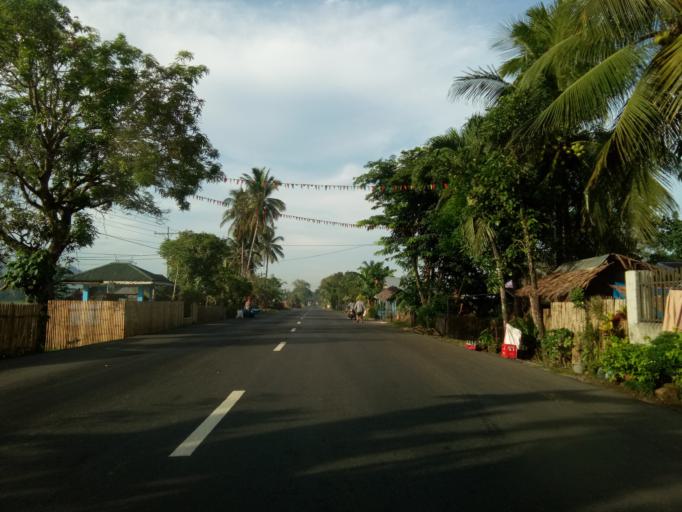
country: PH
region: Caraga
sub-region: Province of Surigao del Norte
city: Tubod
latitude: 9.5465
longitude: 125.5661
